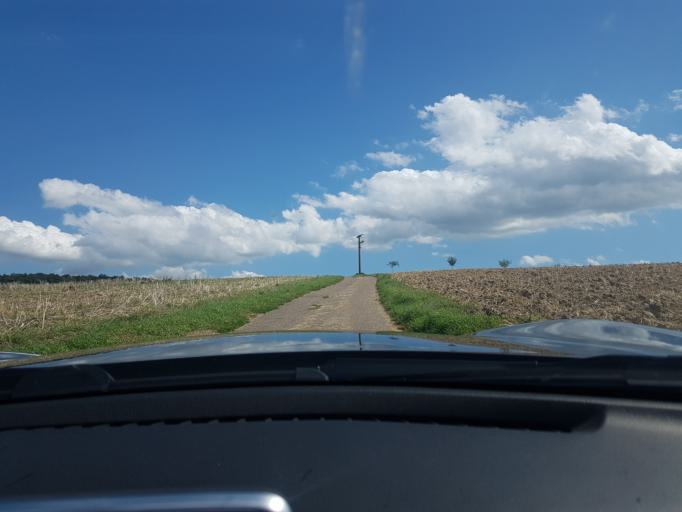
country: DE
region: Baden-Wuerttemberg
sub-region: Regierungsbezirk Stuttgart
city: Widdern
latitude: 49.3421
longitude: 9.3935
